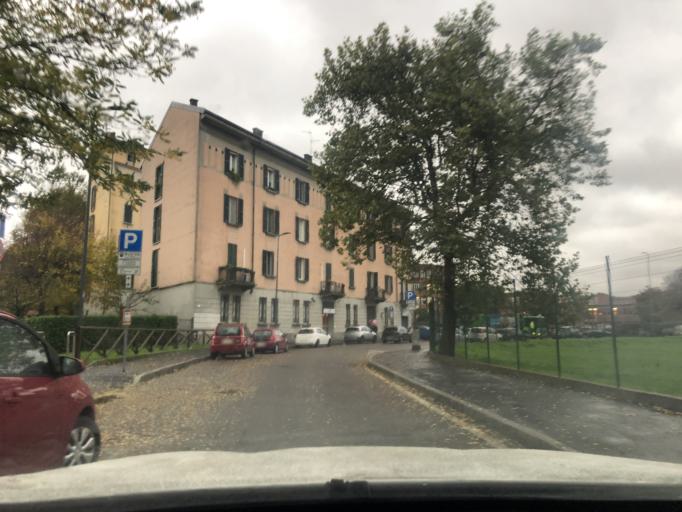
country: IT
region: Lombardy
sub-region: Citta metropolitana di Milano
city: Baranzate
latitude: 45.4875
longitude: 9.1262
